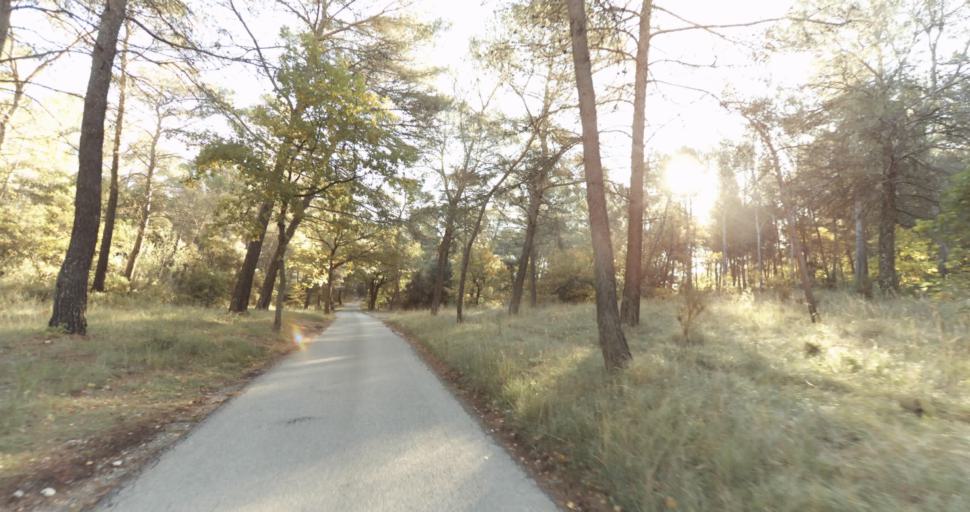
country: FR
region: Provence-Alpes-Cote d'Azur
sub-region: Departement des Bouches-du-Rhone
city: Venelles
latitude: 43.6116
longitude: 5.4725
